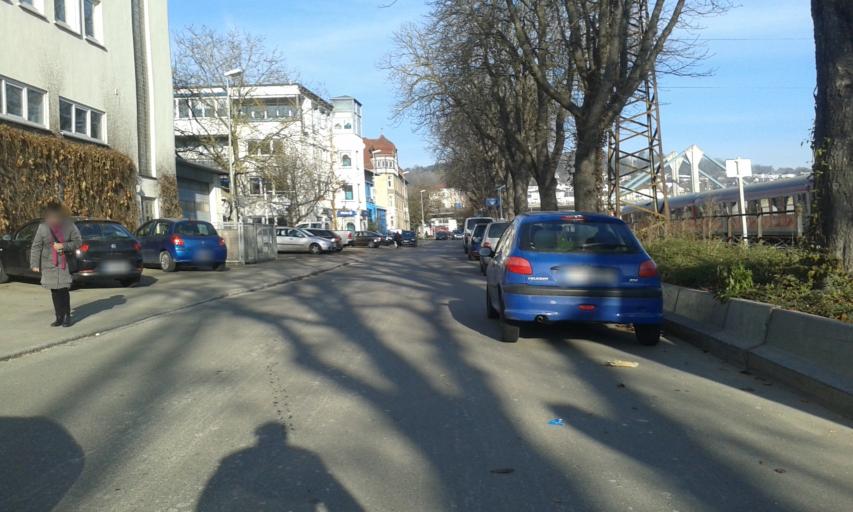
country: DE
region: Baden-Wuerttemberg
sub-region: Tuebingen Region
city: Ulm
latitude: 48.4000
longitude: 9.9813
